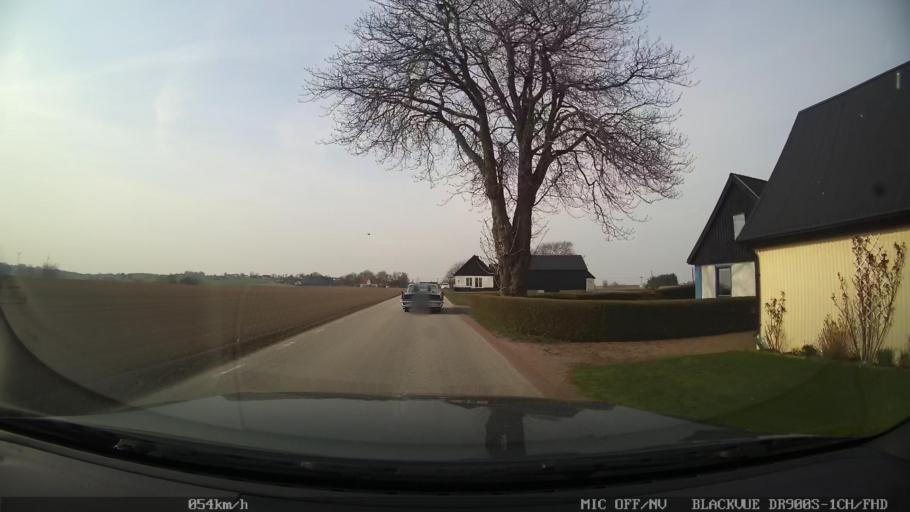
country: SE
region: Skane
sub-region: Ystads Kommun
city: Ystad
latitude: 55.4602
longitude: 13.8259
